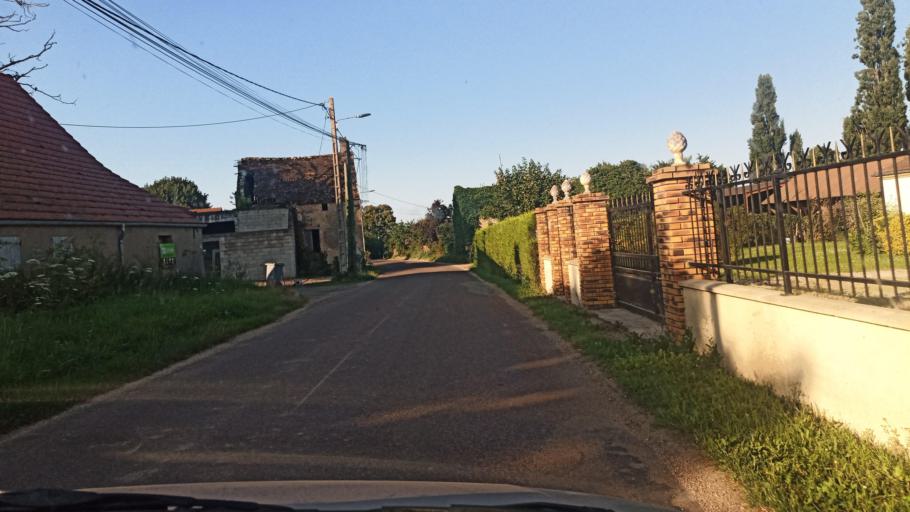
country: FR
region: Bourgogne
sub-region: Departement de l'Yonne
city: Saint-Valerien
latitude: 48.1928
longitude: 3.1197
